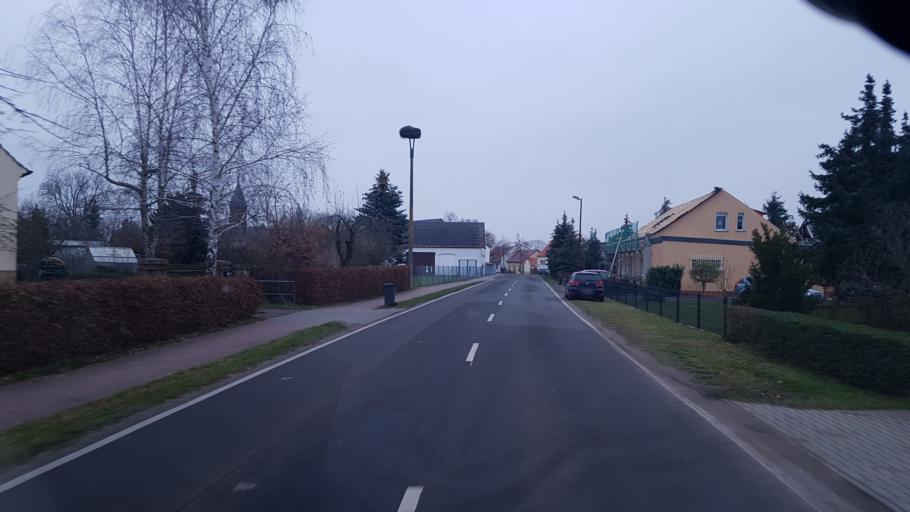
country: DE
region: Brandenburg
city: Drachhausen
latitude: 51.8913
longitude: 14.3182
